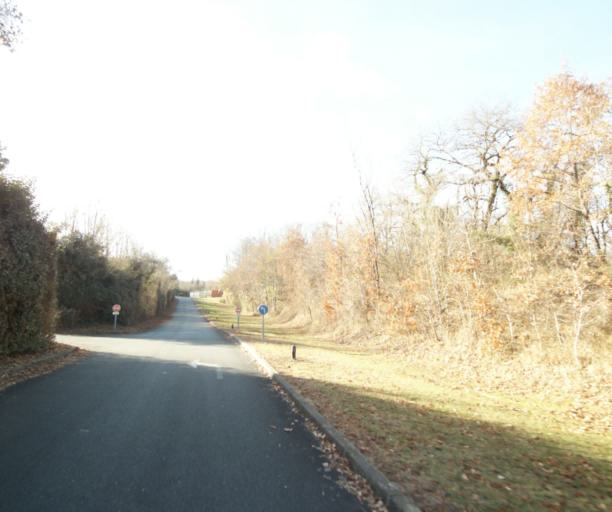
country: FR
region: Poitou-Charentes
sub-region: Departement de la Charente-Maritime
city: Chaniers
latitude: 45.7524
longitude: -0.5031
